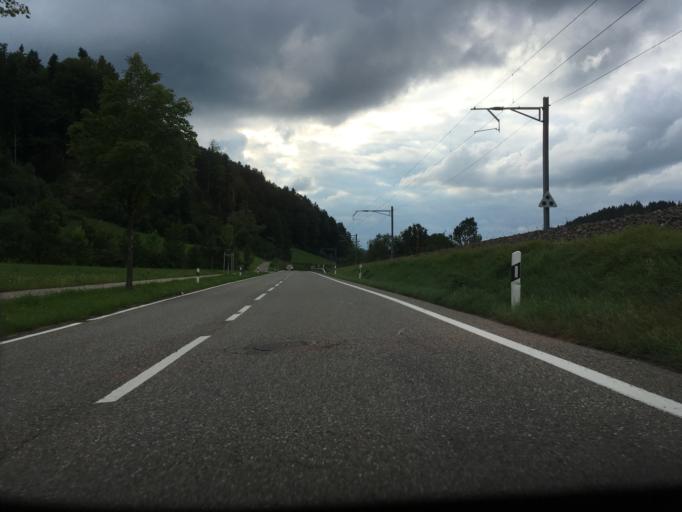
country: CH
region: Zurich
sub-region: Bezirk Pfaeffikon
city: Bauma
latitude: 47.3632
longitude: 8.9086
